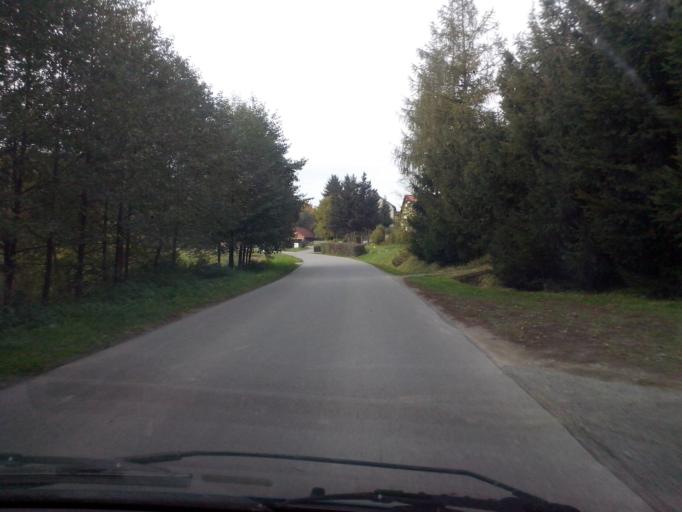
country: PL
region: Subcarpathian Voivodeship
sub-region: Powiat strzyzowski
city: Wisniowa
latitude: 49.8816
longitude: 21.6719
